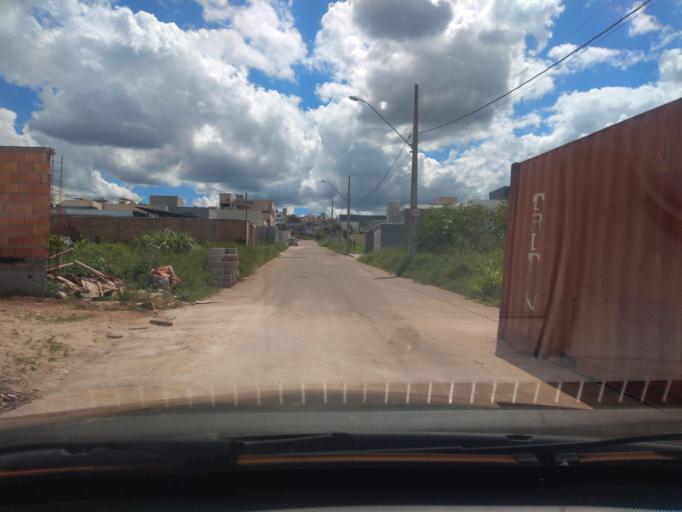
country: BR
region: Minas Gerais
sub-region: Tres Coracoes
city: Tres Coracoes
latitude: -21.6778
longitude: -45.2649
